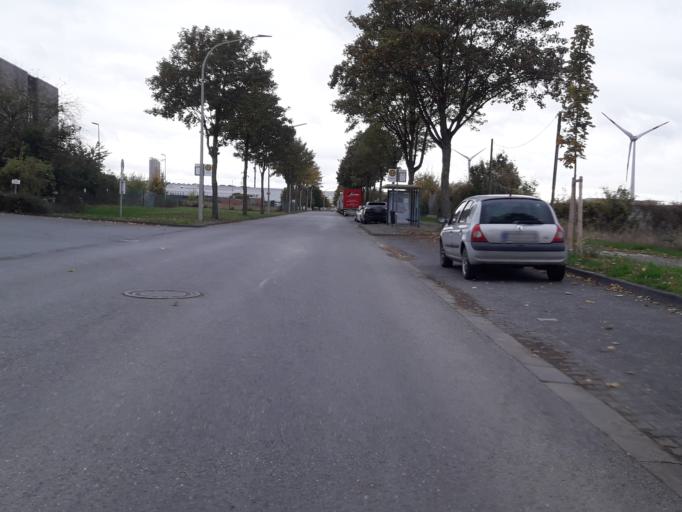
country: DE
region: North Rhine-Westphalia
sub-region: Regierungsbezirk Detmold
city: Paderborn
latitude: 51.6876
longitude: 8.7448
